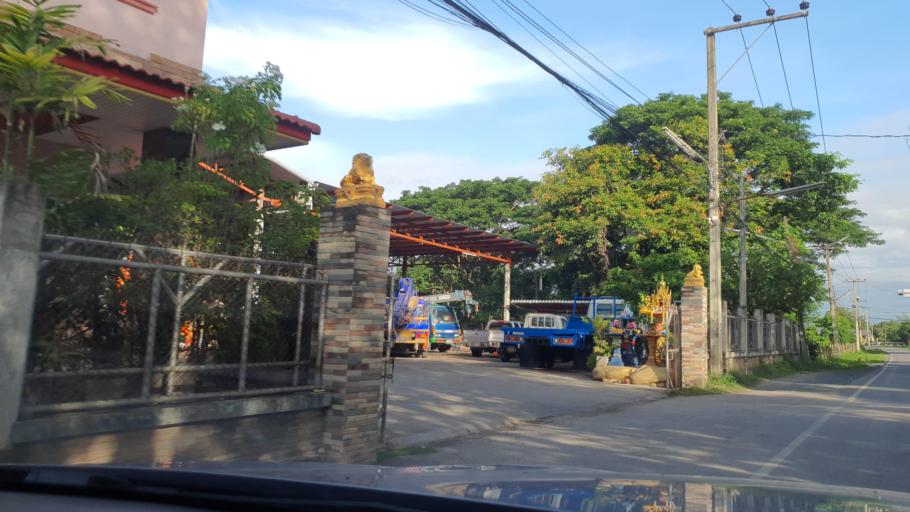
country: TH
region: Chiang Mai
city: San Kamphaeng
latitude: 18.7421
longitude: 99.1029
